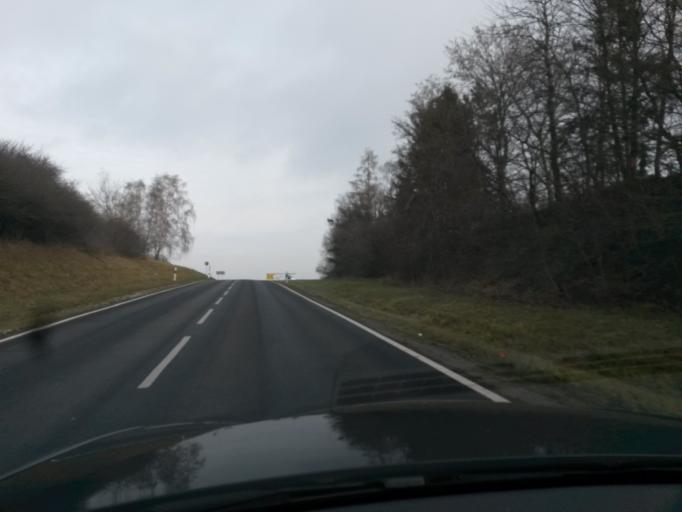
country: DE
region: Bavaria
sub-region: Regierungsbezirk Unterfranken
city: Kurnach
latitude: 49.8454
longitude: 10.0255
